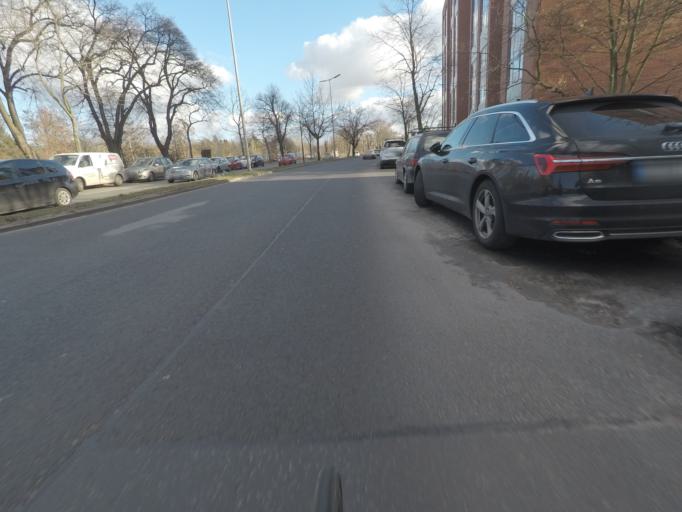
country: DE
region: Berlin
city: Reinickendorf
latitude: 52.5469
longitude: 13.3177
